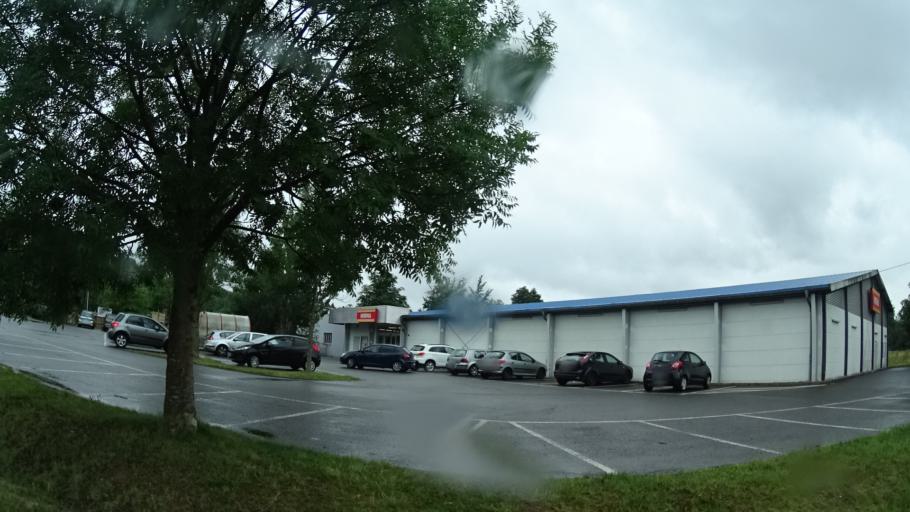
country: DE
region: Saarland
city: Nalbach
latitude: 49.3723
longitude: 6.7936
